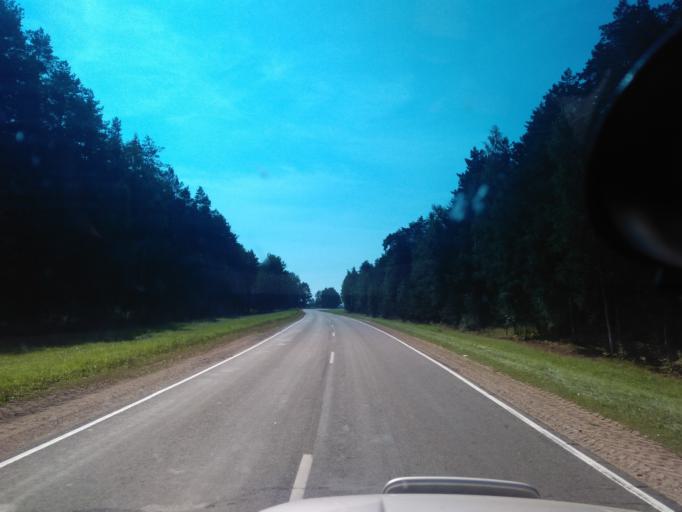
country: BY
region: Minsk
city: Uzda
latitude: 53.4251
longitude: 27.2137
